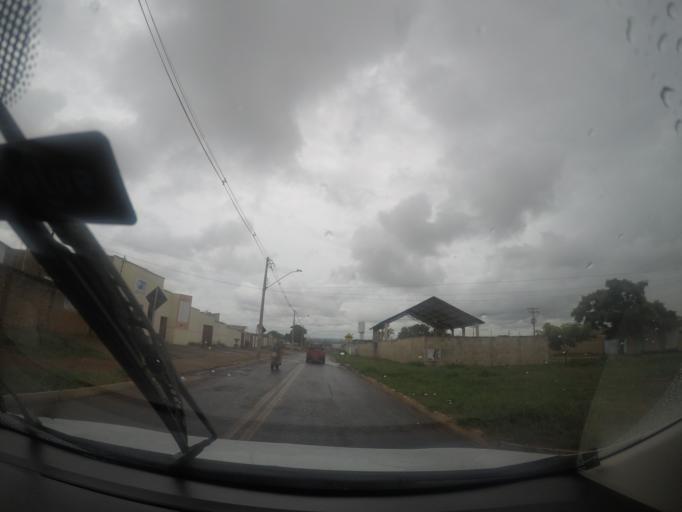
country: BR
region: Goias
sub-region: Trindade
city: Trindade
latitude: -16.6373
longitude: -49.3883
